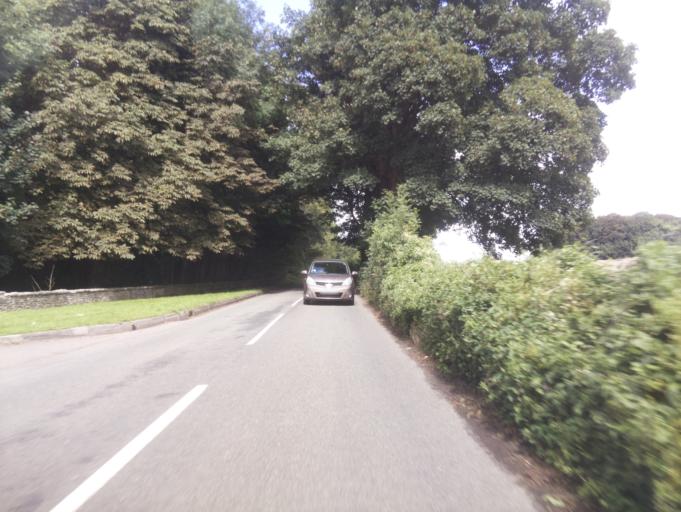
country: GB
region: England
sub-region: Wiltshire
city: Colerne
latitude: 51.4552
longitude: -2.2561
